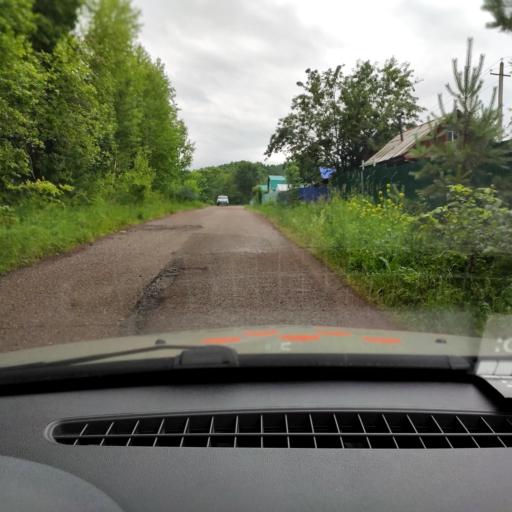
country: RU
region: Bashkortostan
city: Iglino
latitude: 54.8866
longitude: 56.2692
